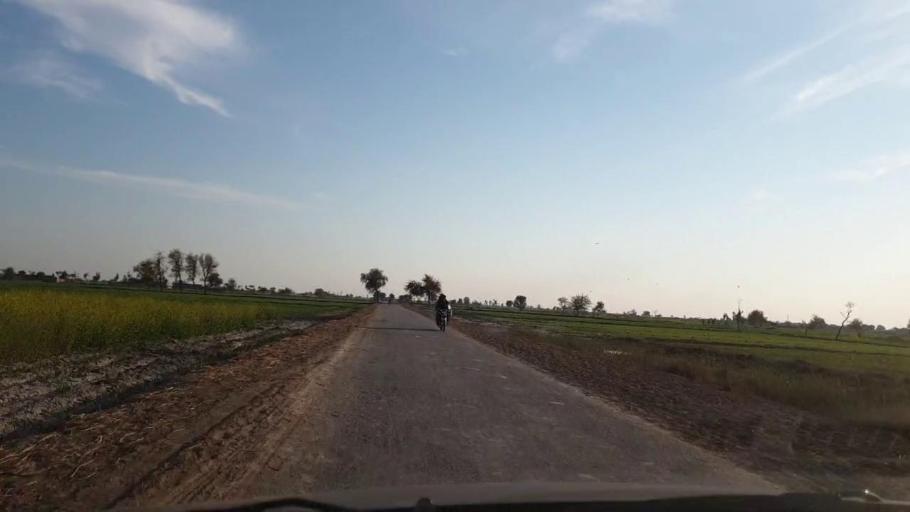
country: PK
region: Sindh
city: Khadro
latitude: 26.1683
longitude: 68.7532
